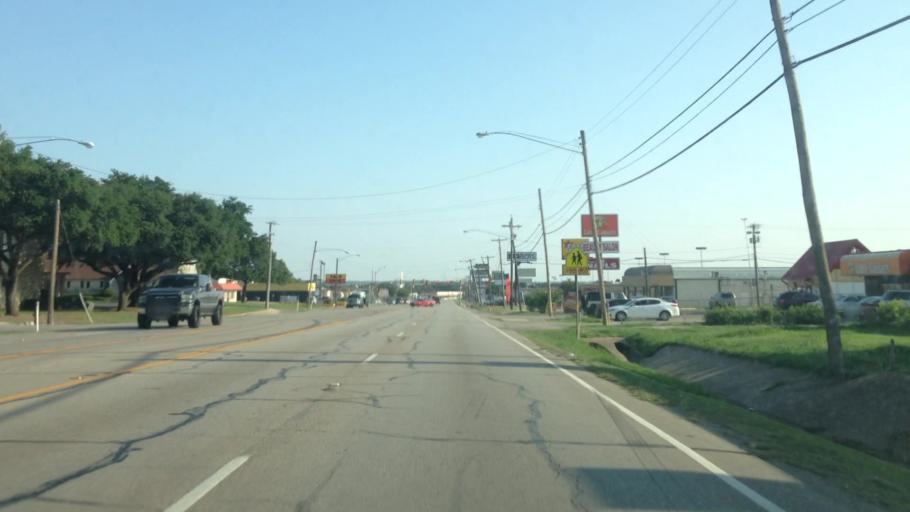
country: US
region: Texas
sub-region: Tarrant County
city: Haltom City
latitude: 32.8077
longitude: -97.2646
